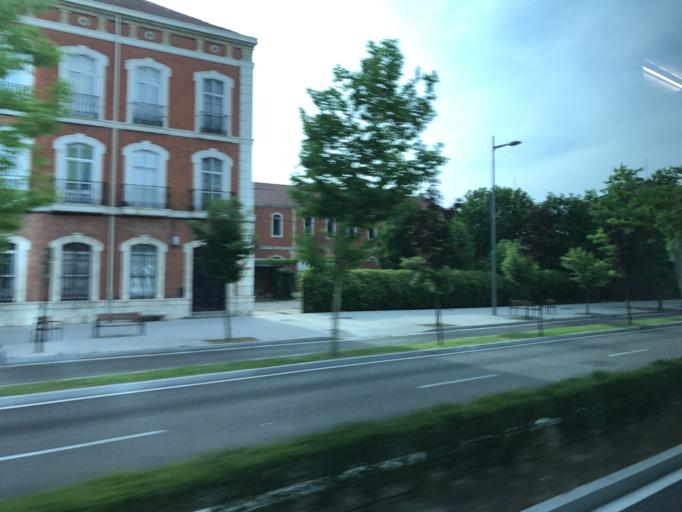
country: ES
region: Castille and Leon
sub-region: Provincia de Valladolid
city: Valladolid
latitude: 41.6343
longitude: -4.7290
